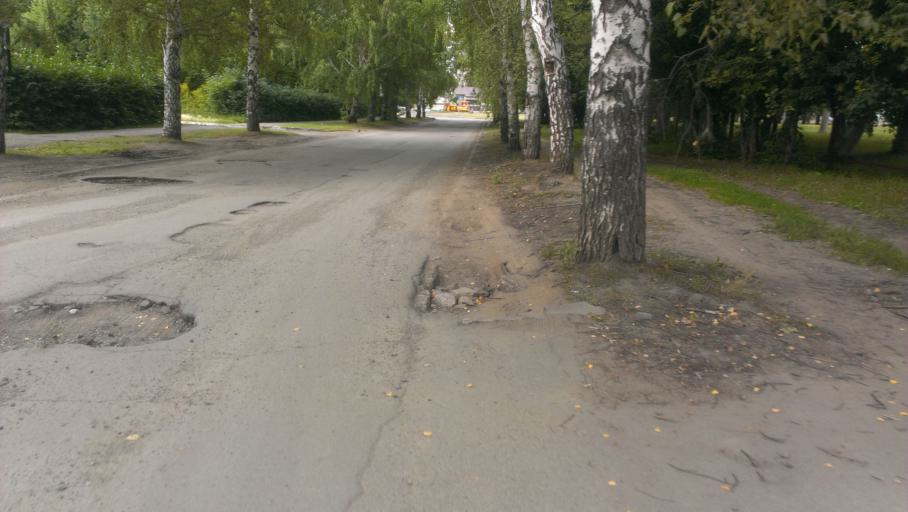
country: RU
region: Altai Krai
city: Yuzhnyy
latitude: 53.2528
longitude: 83.6926
